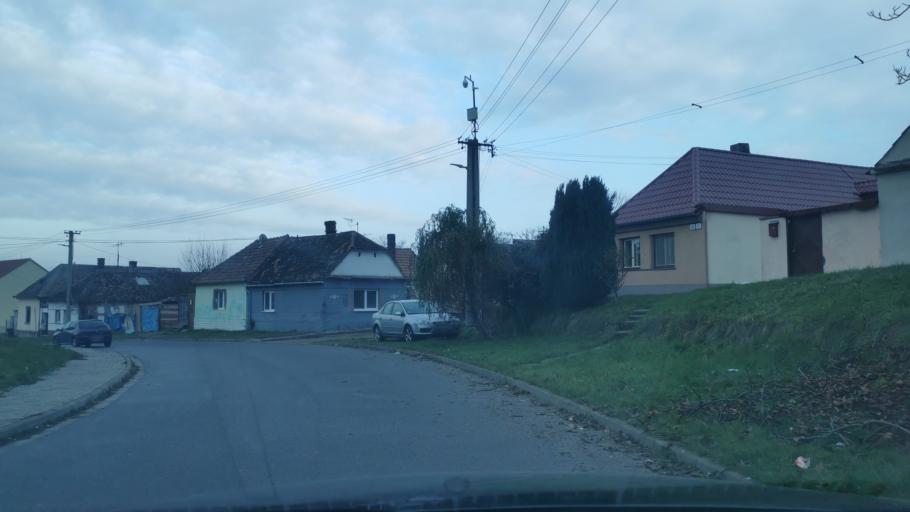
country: SK
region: Trnavsky
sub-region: Okres Skalica
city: Holic
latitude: 48.8075
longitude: 17.1671
